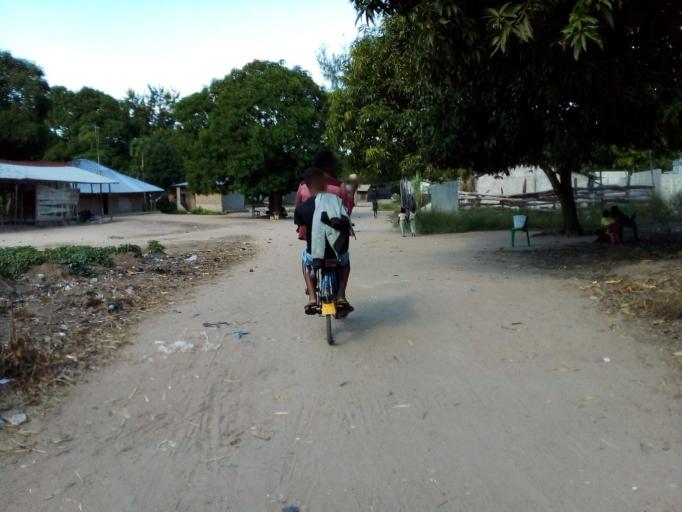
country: MZ
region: Zambezia
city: Quelimane
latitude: -17.6039
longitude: 36.8208
